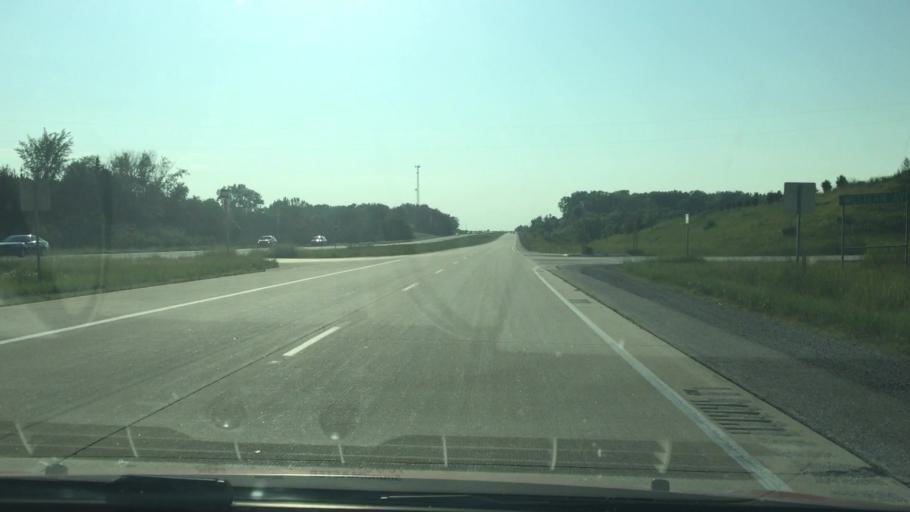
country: US
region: Iowa
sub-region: Scott County
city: Blue Grass
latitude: 41.5175
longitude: -90.8424
